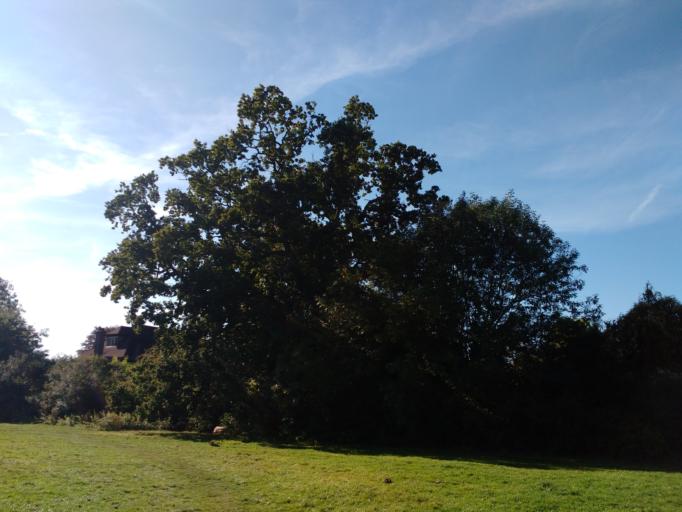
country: GB
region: England
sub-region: Bristol
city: Bristol
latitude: 51.4878
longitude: -2.6373
